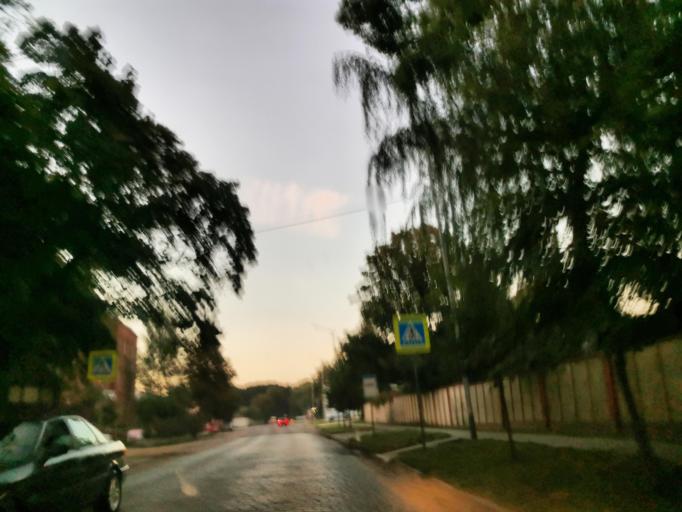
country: RU
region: Kaliningrad
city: Chernyakhovsk
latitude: 54.6444
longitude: 21.8088
